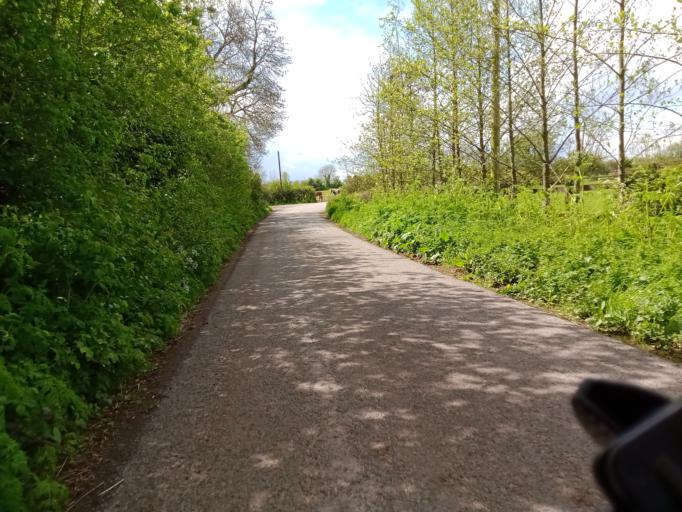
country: IE
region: Leinster
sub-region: Kilkenny
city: Thomastown
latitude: 52.5860
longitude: -7.1421
